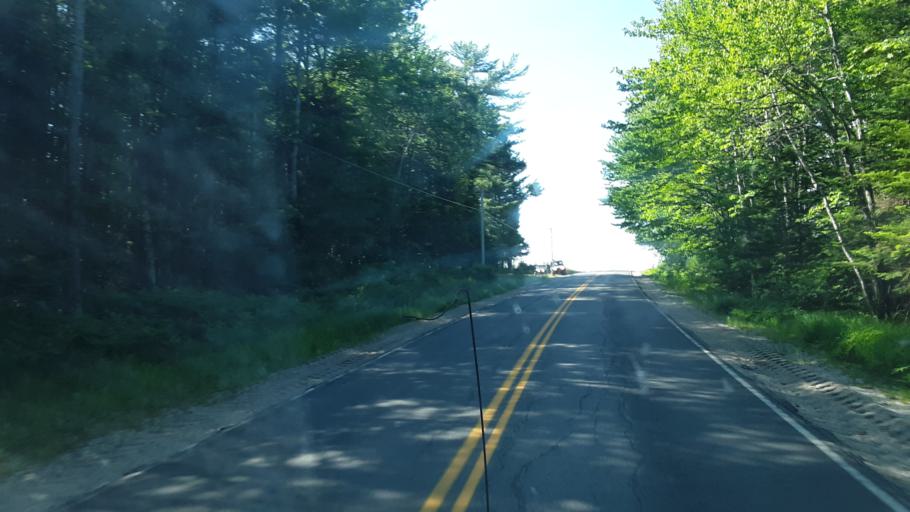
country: US
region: Maine
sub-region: Washington County
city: Cherryfield
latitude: 44.7590
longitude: -68.0256
